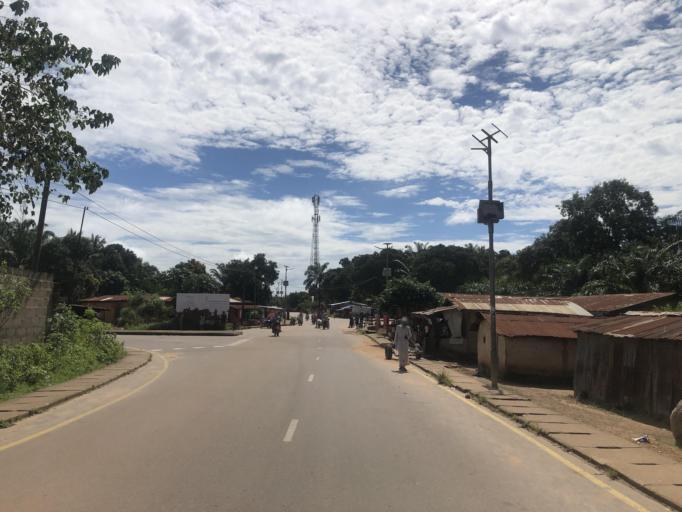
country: SL
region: Eastern Province
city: Koidu
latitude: 8.6385
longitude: -10.9702
